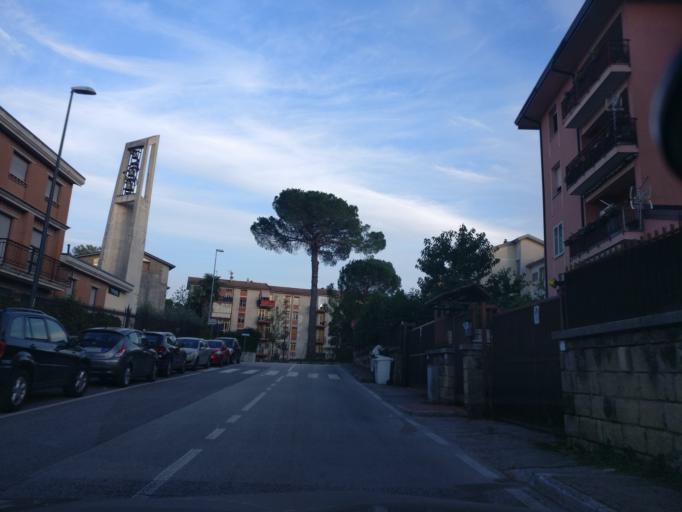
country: IT
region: Campania
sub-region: Provincia di Avellino
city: Avellino
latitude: 40.9093
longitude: 14.7923
